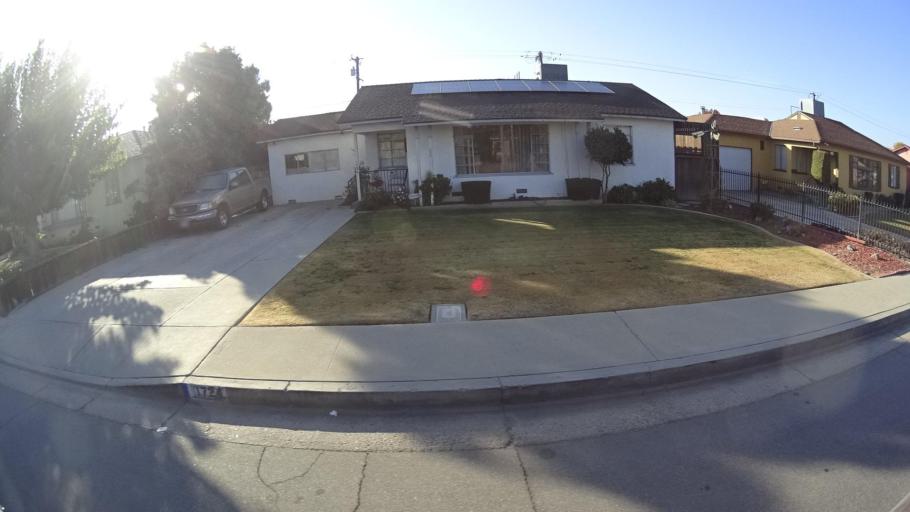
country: US
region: California
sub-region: Kern County
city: Delano
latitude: 35.7686
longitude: -119.2332
